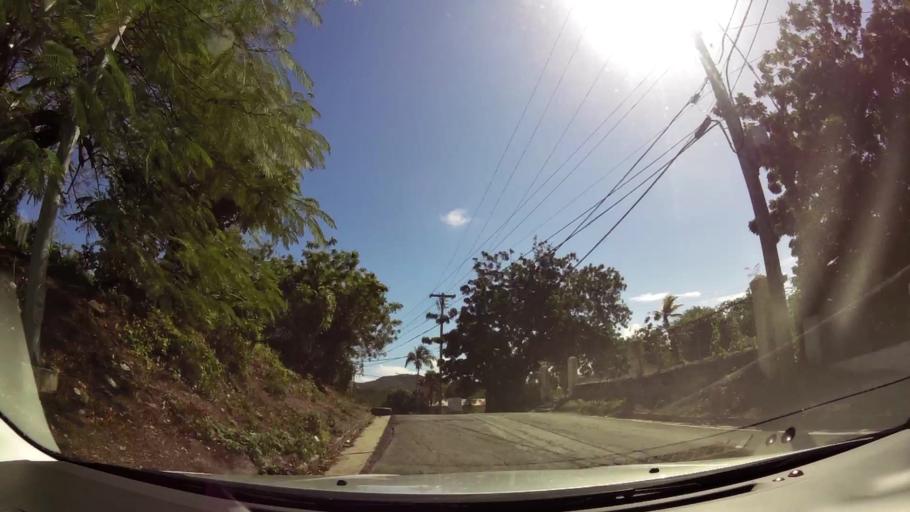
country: AG
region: Saint Paul
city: Falmouth
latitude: 17.0166
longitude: -61.7658
